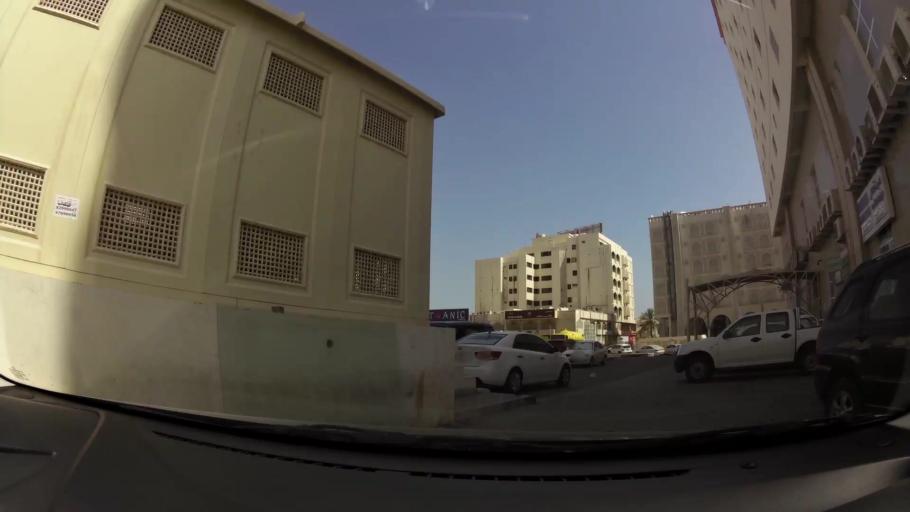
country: OM
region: Muhafazat Masqat
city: Bawshar
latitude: 23.5955
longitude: 58.4268
